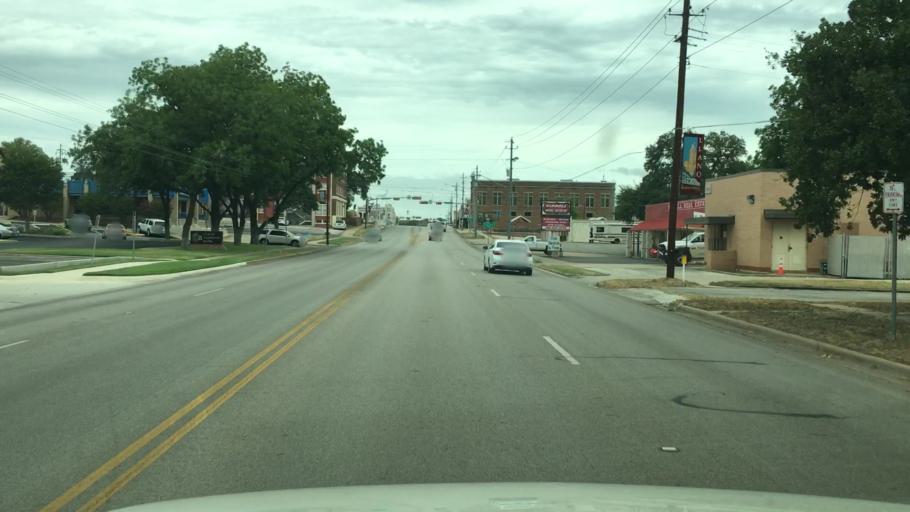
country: US
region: Texas
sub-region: Llano County
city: Llano
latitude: 30.7475
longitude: -98.6759
